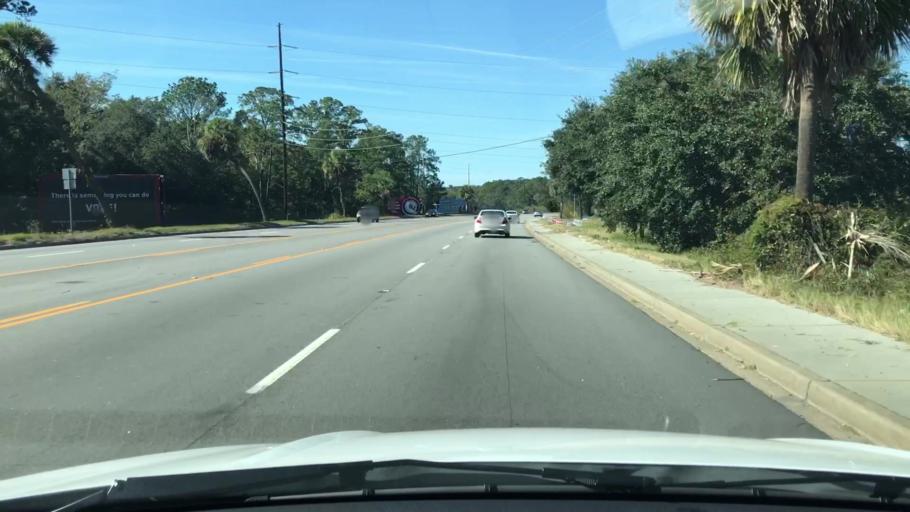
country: US
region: South Carolina
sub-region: Beaufort County
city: Burton
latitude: 32.4434
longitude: -80.7259
